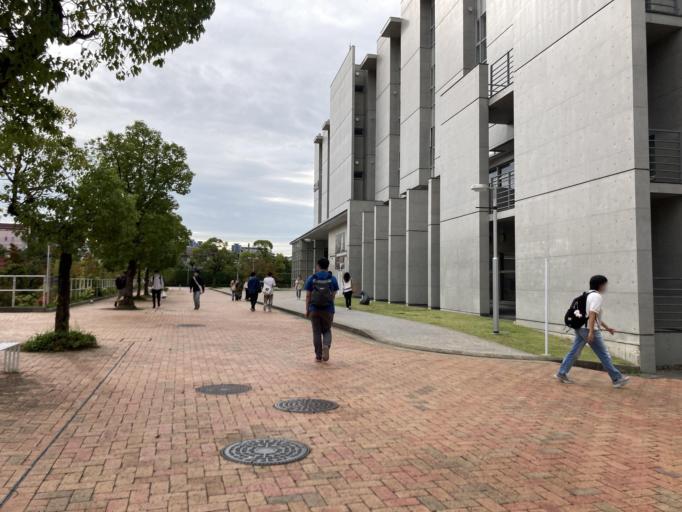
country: JP
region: Fukuoka
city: Shingu
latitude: 33.6715
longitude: 130.4442
